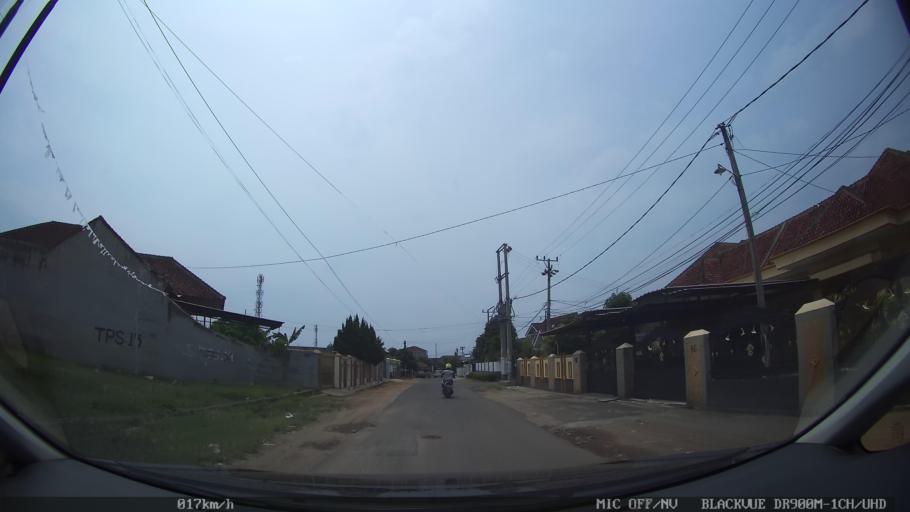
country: ID
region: Lampung
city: Bandarlampung
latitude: -5.4189
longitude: 105.2744
